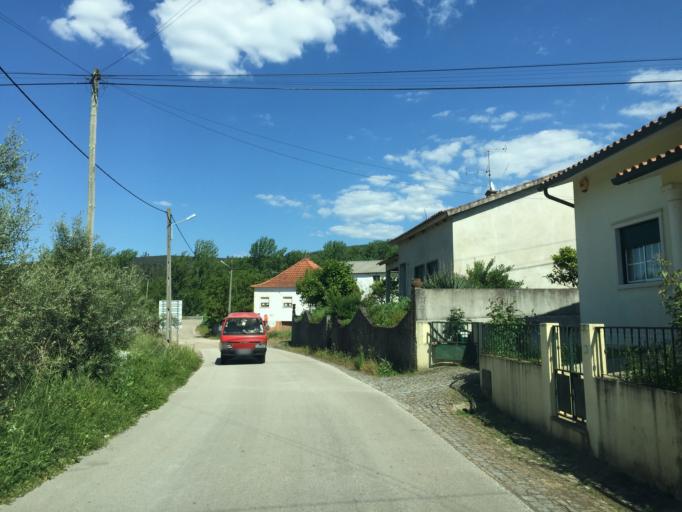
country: PT
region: Leiria
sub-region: Alvaiazere
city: Alvaiazere
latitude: 39.8472
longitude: -8.3492
